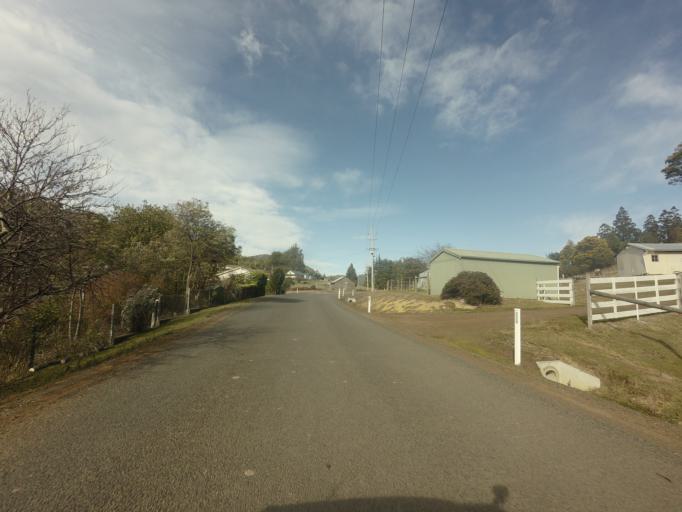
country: AU
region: Tasmania
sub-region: Kingborough
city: Margate
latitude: -43.0191
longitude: 147.1646
